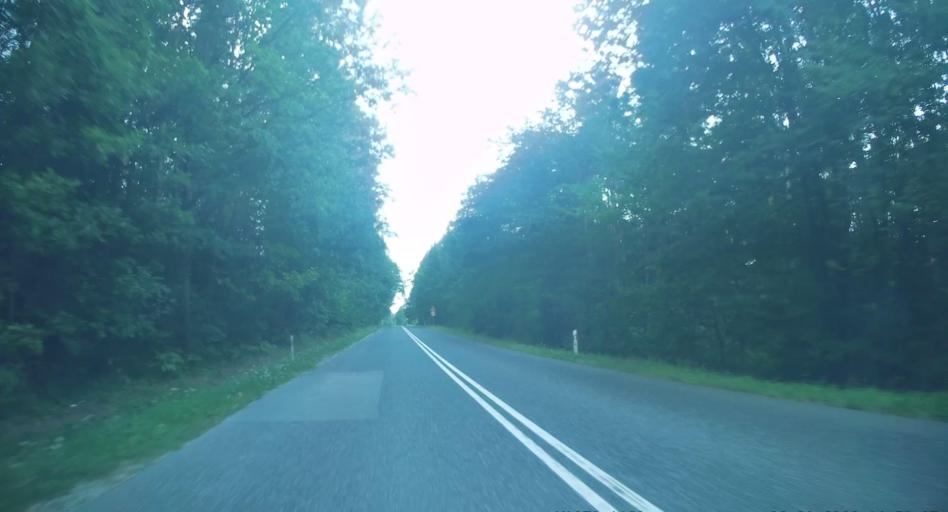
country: PL
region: Swietokrzyskie
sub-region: Powiat kielecki
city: Lopuszno
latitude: 50.8871
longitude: 20.2595
